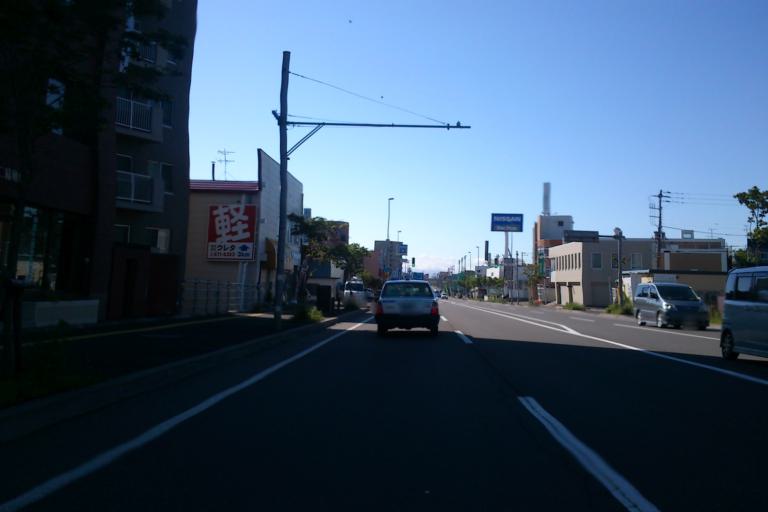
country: JP
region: Hokkaido
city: Sapporo
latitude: 43.1189
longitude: 141.2392
